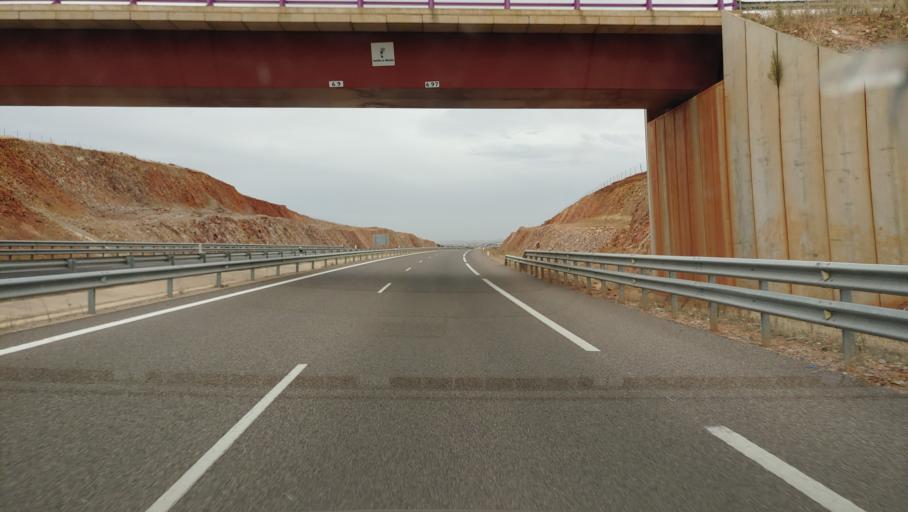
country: ES
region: Castille-La Mancha
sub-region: Provincia de Ciudad Real
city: Valenzuela de Calatrava
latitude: 38.8958
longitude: -3.7681
